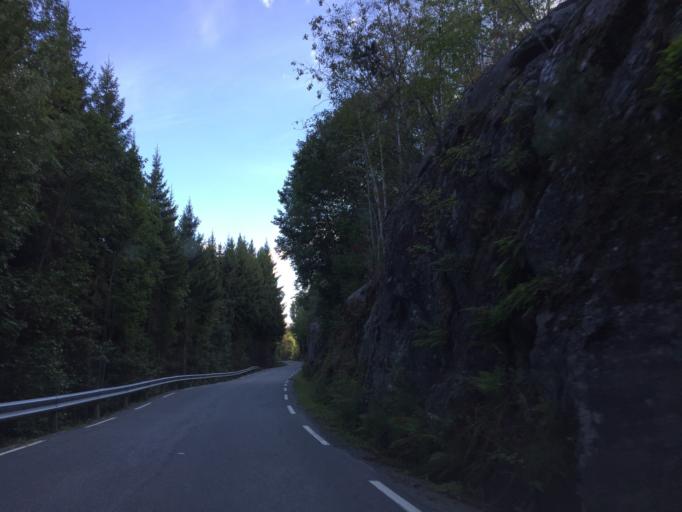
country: NO
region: Buskerud
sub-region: Ovre Eiker
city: Hokksund
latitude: 59.6515
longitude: 9.9160
